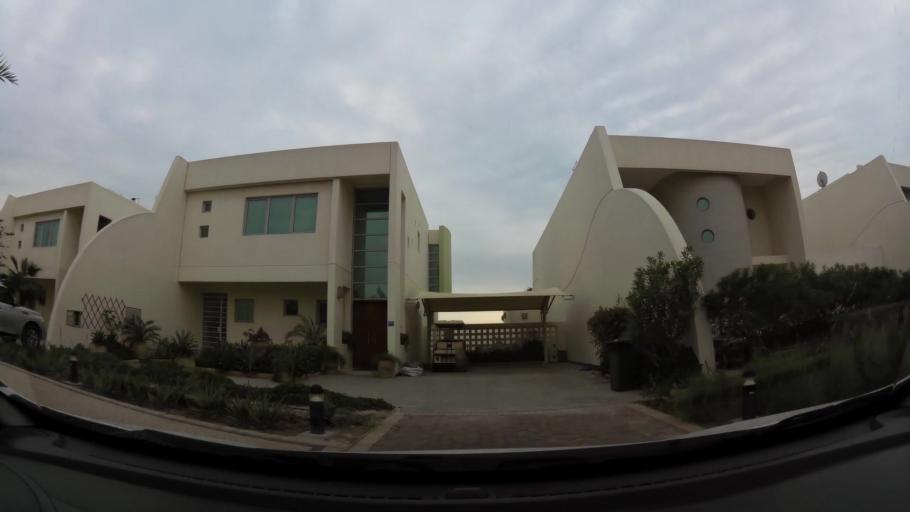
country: BH
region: Central Governorate
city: Dar Kulayb
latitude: 25.8325
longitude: 50.6156
